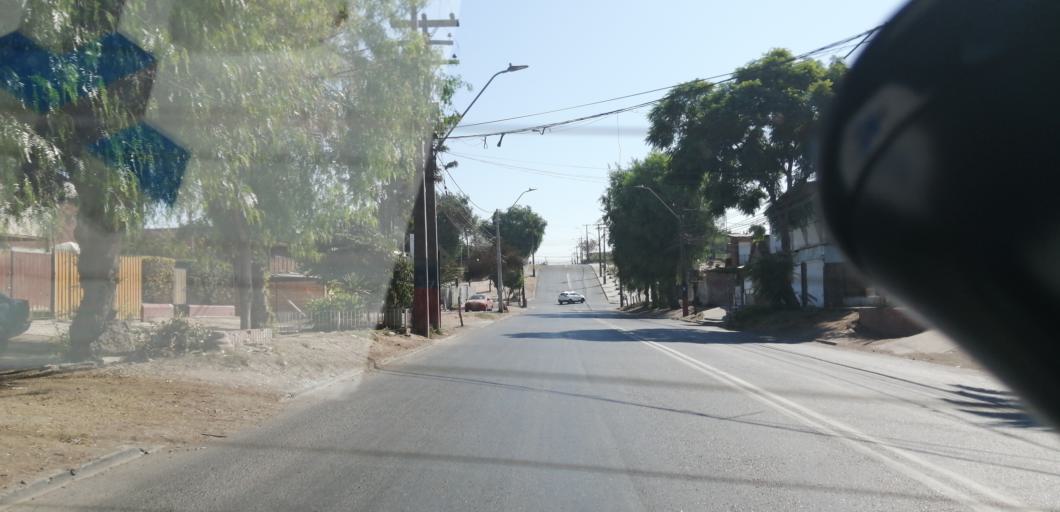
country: CL
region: Santiago Metropolitan
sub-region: Provincia de Santiago
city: Lo Prado
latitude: -33.4483
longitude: -70.7543
